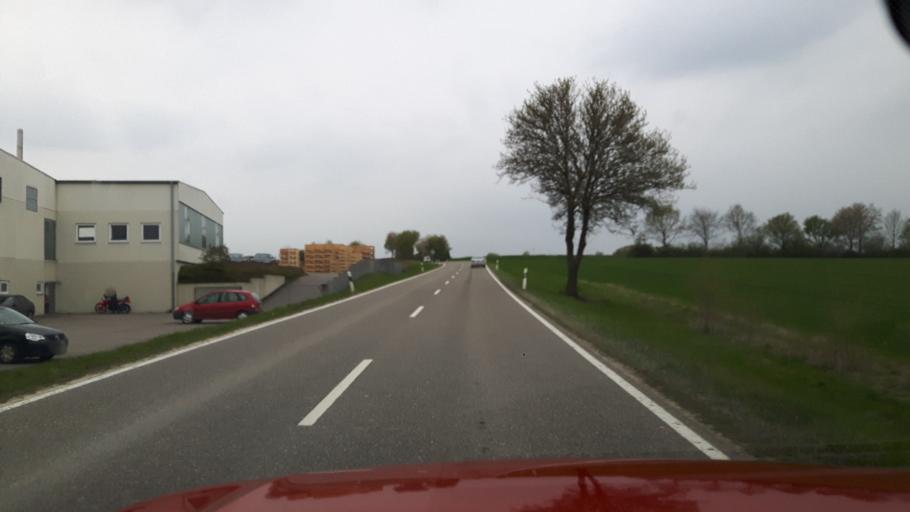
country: DE
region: Bavaria
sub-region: Upper Bavaria
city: Eichstaett
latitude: 48.9098
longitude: 11.1695
